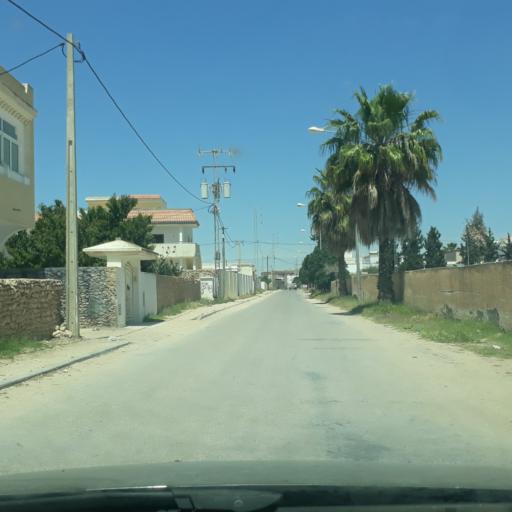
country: TN
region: Safaqis
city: Al Qarmadah
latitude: 34.8132
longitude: 10.7585
